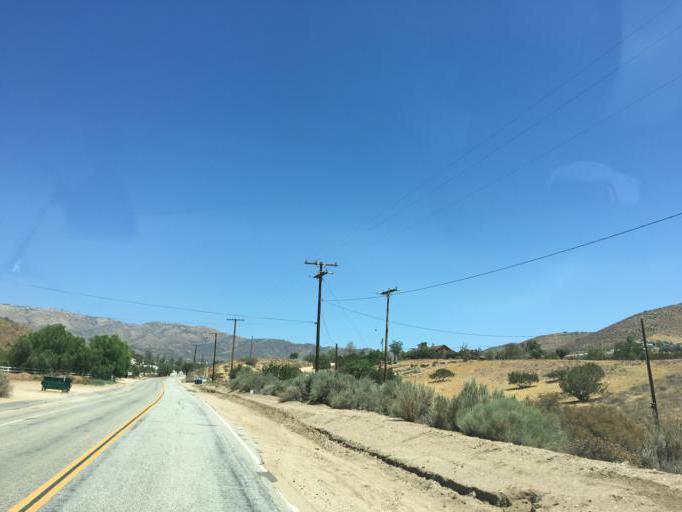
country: US
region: California
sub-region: Los Angeles County
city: Acton
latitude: 34.5012
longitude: -118.2185
